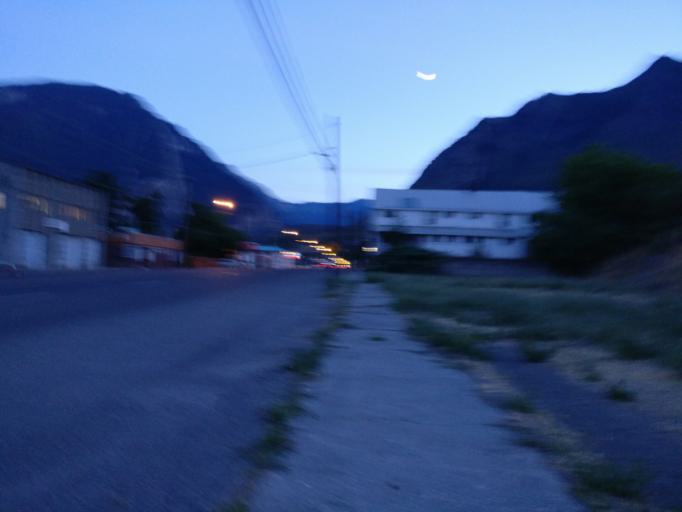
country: CA
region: British Columbia
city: Lillooet
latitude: 50.6951
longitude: -121.9314
